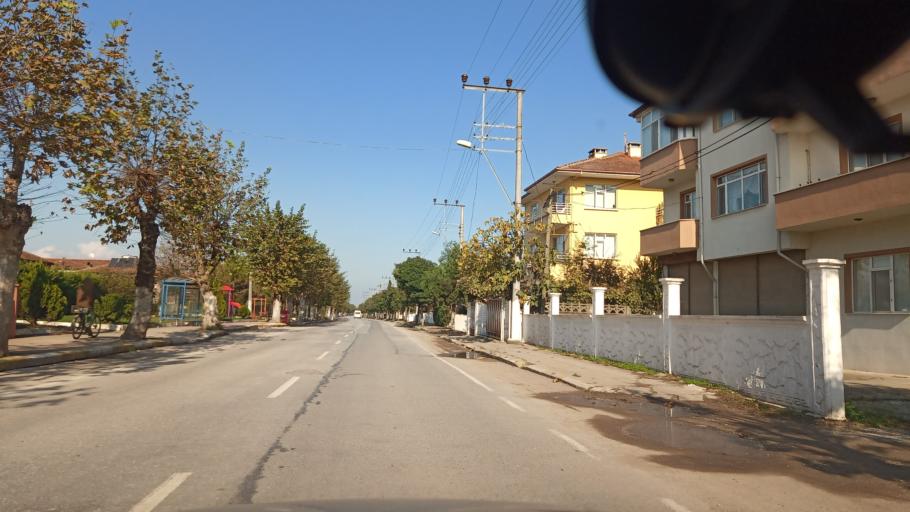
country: TR
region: Sakarya
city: Sogutlu
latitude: 40.8818
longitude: 30.4632
